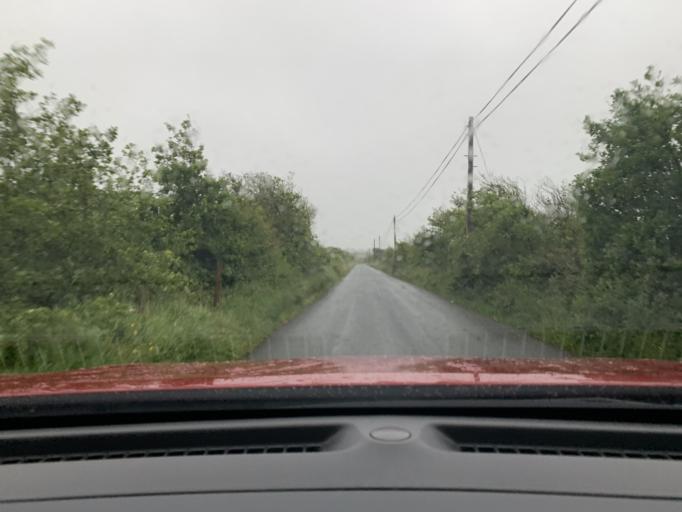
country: IE
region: Connaught
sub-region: County Leitrim
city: Kinlough
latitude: 54.4510
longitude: -8.4507
